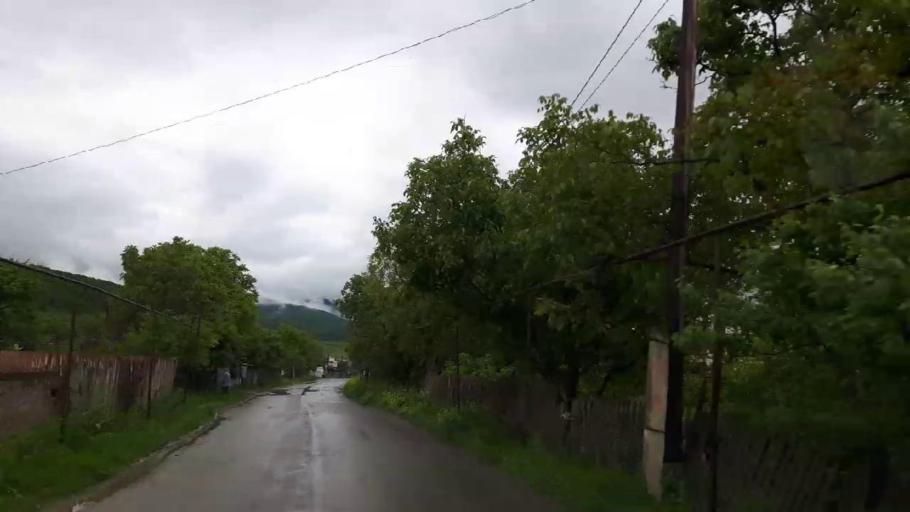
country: GE
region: Shida Kartli
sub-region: Khashuris Raioni
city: Khashuri
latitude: 41.9834
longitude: 43.6654
